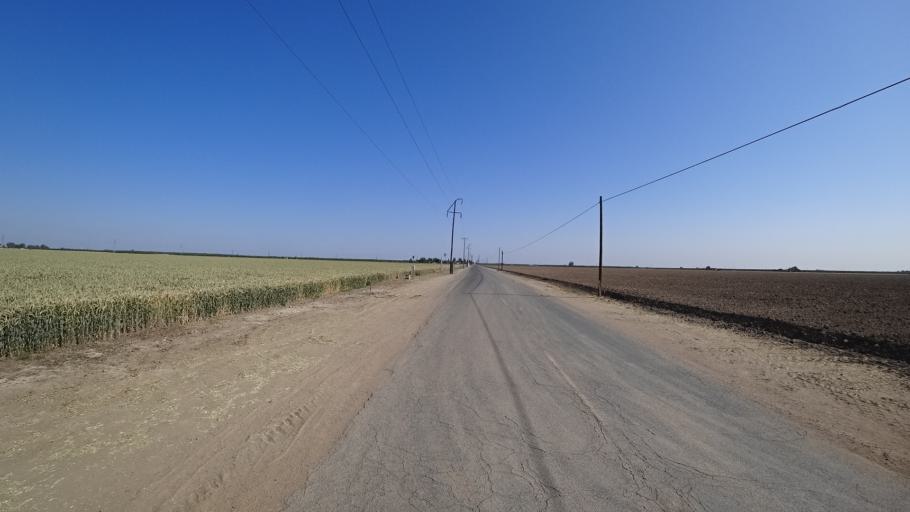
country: US
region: California
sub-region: Kings County
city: Home Garden
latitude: 36.2478
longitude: -119.5831
